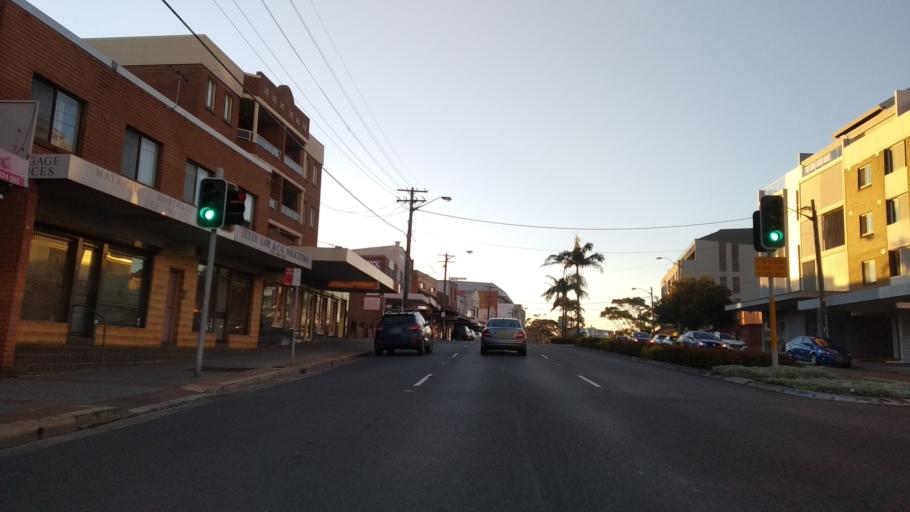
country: AU
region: New South Wales
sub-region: Randwick
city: Maroubra
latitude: -33.9576
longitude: 151.2308
